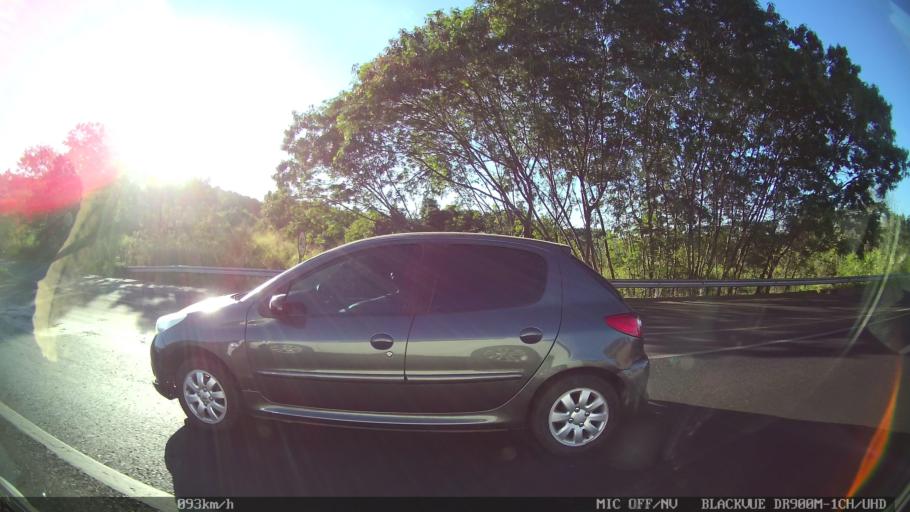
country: BR
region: Sao Paulo
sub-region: Guapiacu
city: Guapiacu
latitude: -20.7837
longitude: -49.2687
